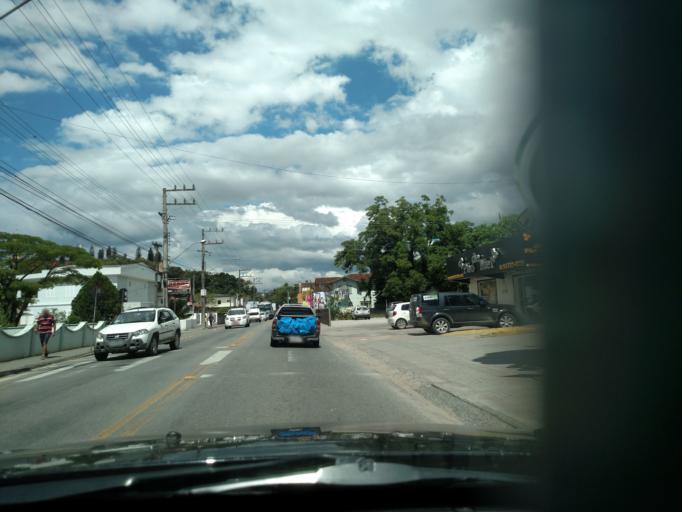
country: BR
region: Santa Catarina
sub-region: Gaspar
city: Gaspar
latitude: -26.9291
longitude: -48.9622
